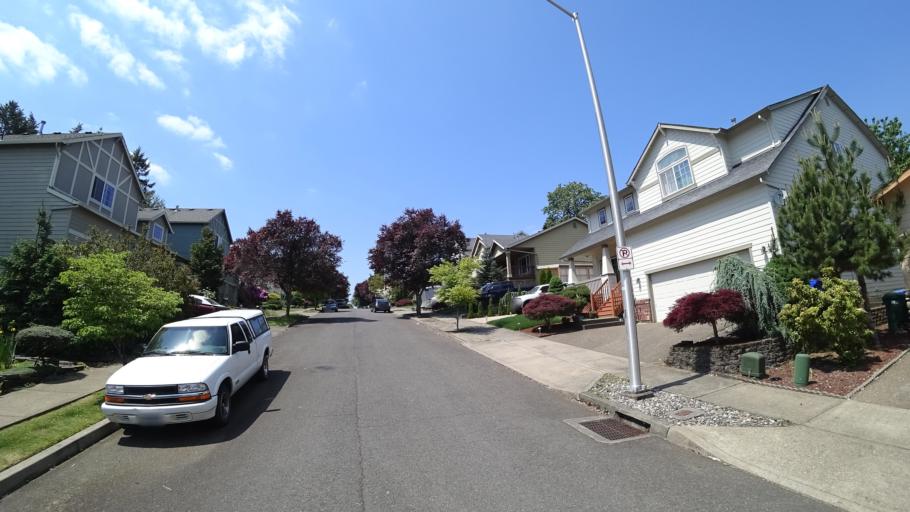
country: US
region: Oregon
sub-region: Clackamas County
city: Happy Valley
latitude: 45.4734
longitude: -122.5027
